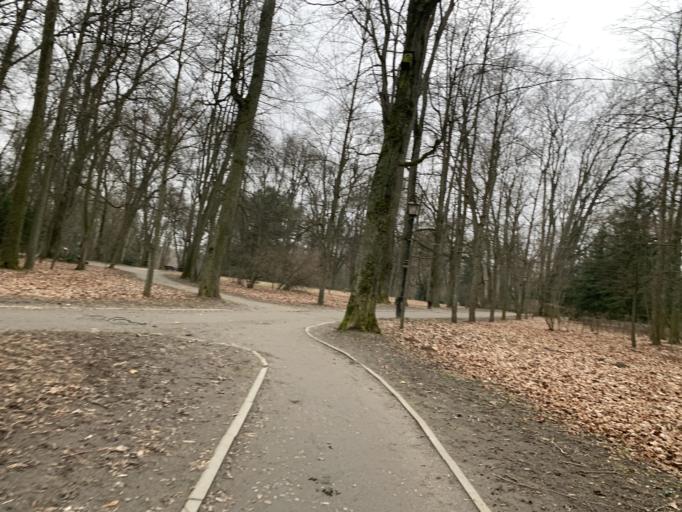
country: BY
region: Minsk
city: Nyasvizh
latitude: 53.2273
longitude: 26.6928
